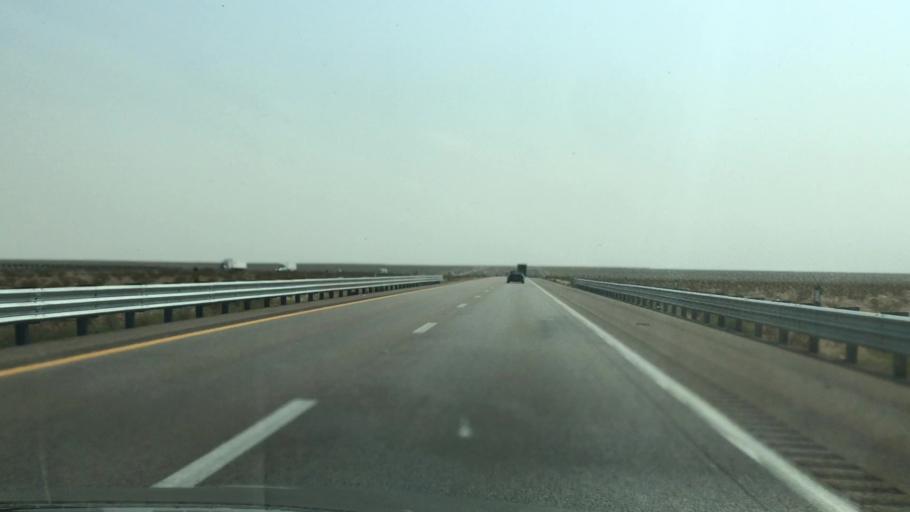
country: US
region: Nevada
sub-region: Clark County
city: Bunkerville
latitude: 36.7722
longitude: -114.2991
